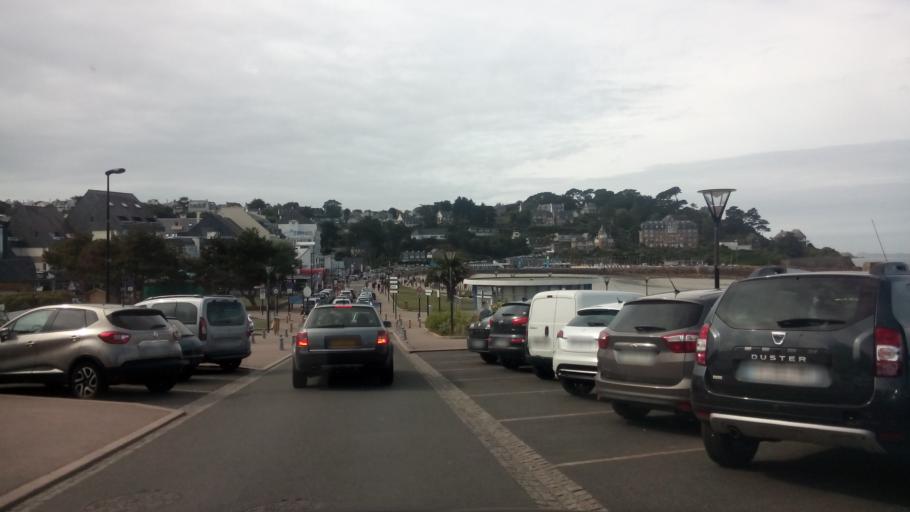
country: FR
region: Brittany
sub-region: Departement des Cotes-d'Armor
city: Perros-Guirec
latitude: 48.8151
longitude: -3.4555
